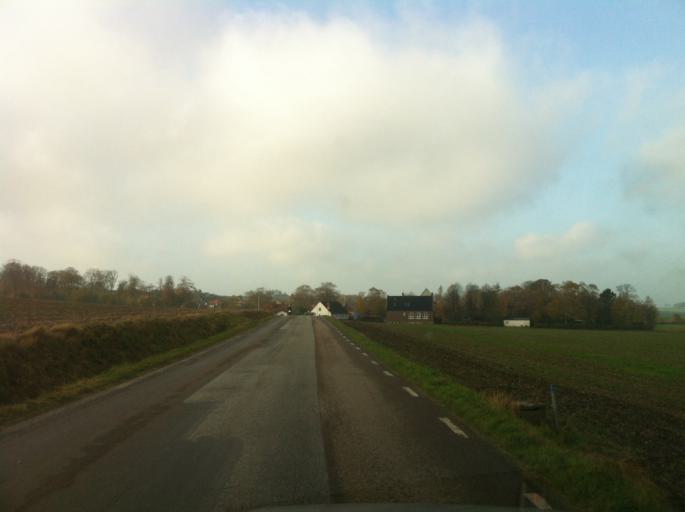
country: SE
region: Skane
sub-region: Helsingborg
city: Glumslov
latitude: 55.9320
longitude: 12.8817
